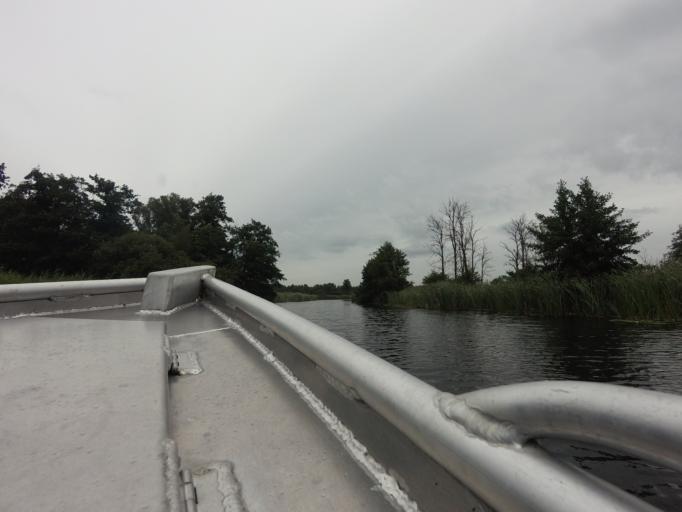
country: NL
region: Overijssel
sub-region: Gemeente Steenwijkerland
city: Giethoorn
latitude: 52.7284
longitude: 6.0338
